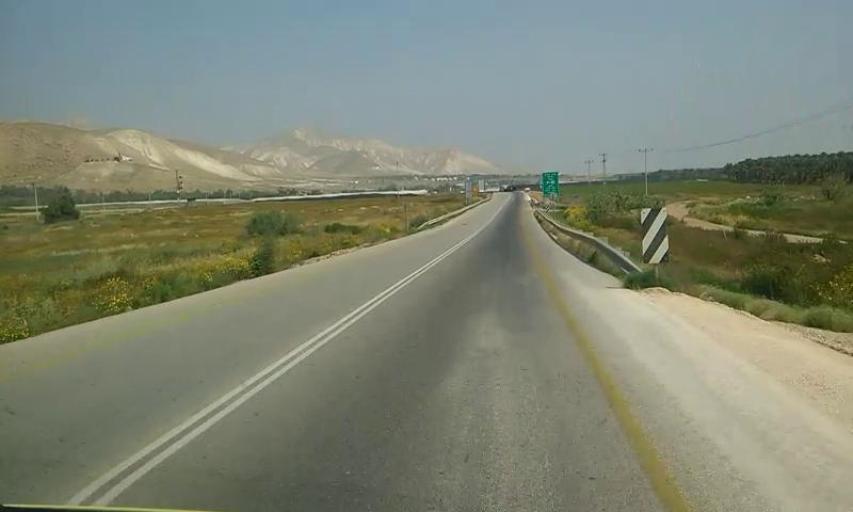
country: PS
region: West Bank
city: Al Fasayil
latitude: 32.0444
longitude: 35.4617
